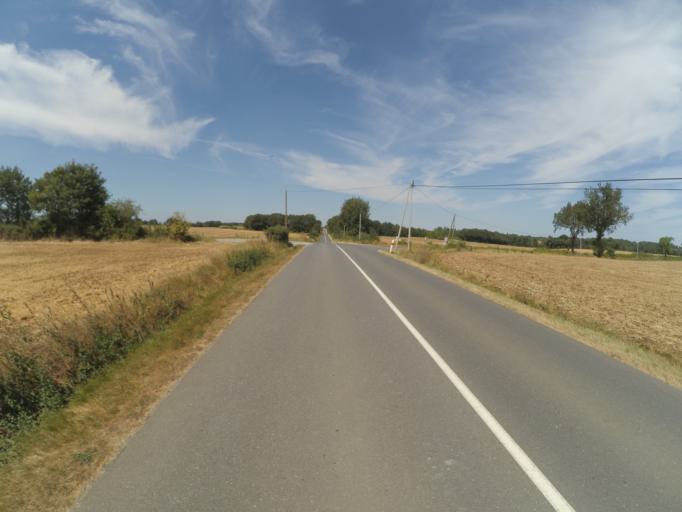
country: FR
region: Poitou-Charentes
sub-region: Departement de la Vienne
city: Usson-du-Poitou
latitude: 46.2322
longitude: 0.5280
